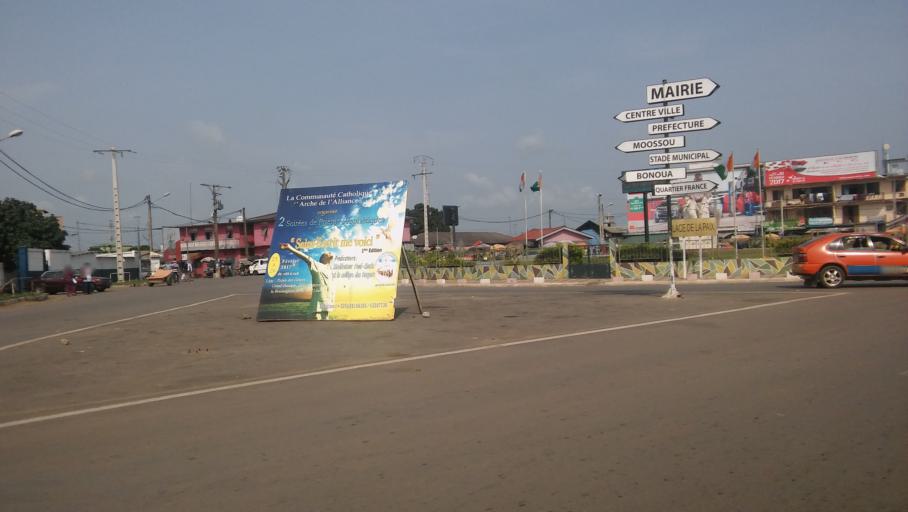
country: CI
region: Sud-Comoe
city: Grand-Bassam
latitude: 5.2068
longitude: -3.7360
